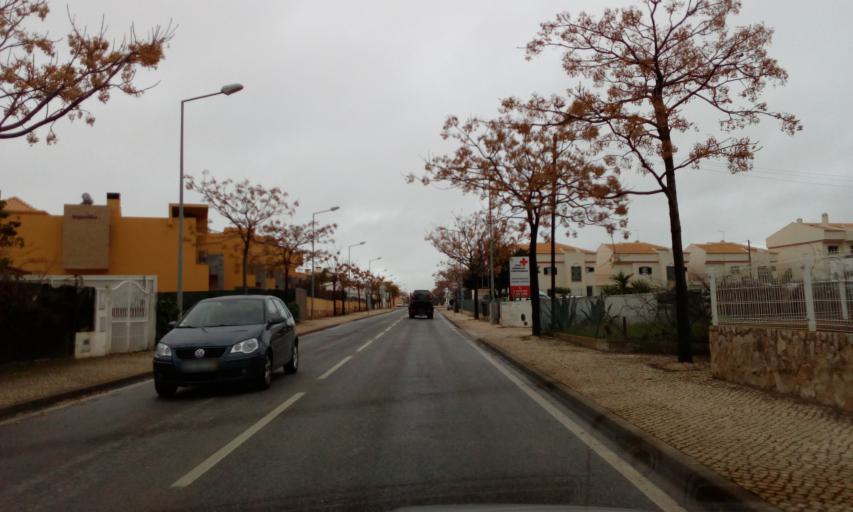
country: PT
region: Faro
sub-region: Albufeira
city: Ferreiras
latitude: 37.1290
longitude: -8.2523
